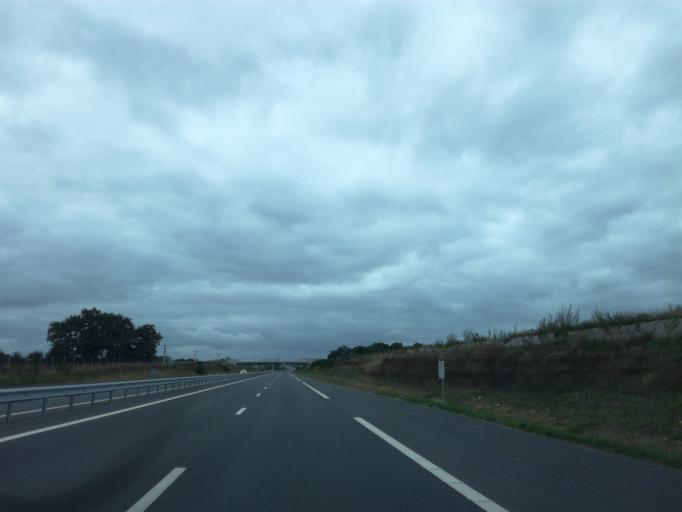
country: FR
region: Brittany
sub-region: Departement d'Ille-et-Vilaine
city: Boisgervilly
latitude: 48.1908
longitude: -2.1149
